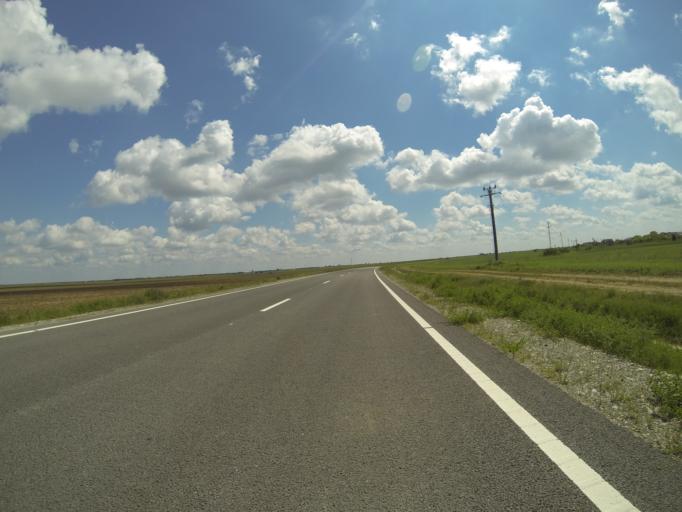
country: RO
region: Dolj
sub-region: Comuna Carcea
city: Carcea
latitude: 44.2714
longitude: 23.9118
